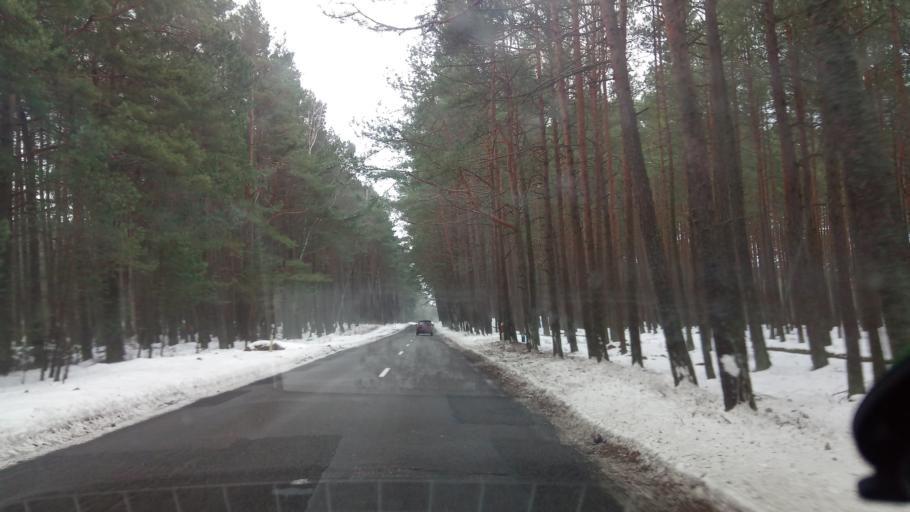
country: LT
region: Klaipedos apskritis
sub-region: Klaipeda
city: Klaipeda
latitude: 55.5938
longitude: 21.1293
